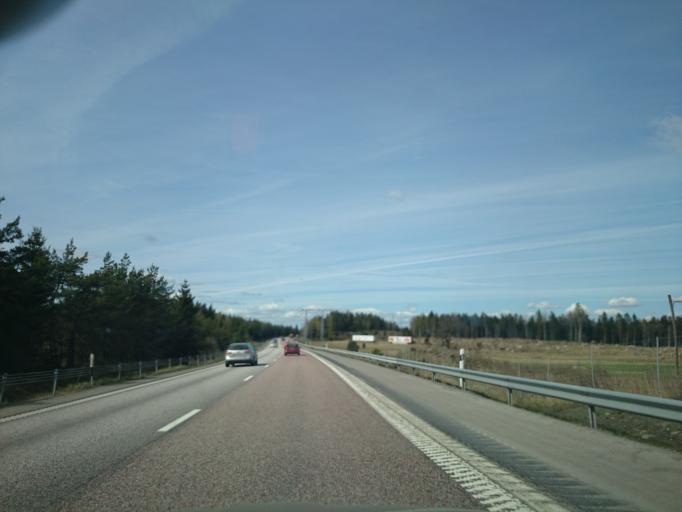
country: SE
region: Uppsala
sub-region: Knivsta Kommun
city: Knivsta
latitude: 59.7592
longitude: 17.8015
